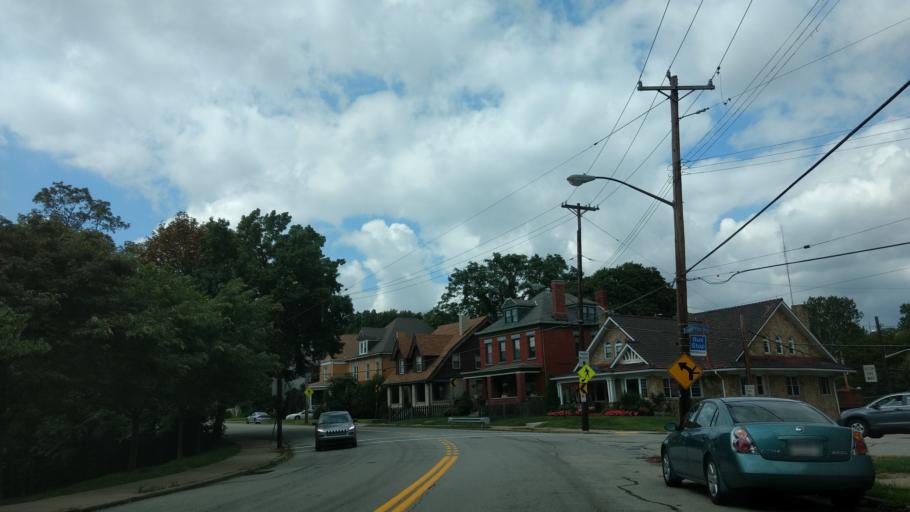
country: US
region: Pennsylvania
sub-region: Allegheny County
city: Millvale
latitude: 40.4840
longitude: -80.0133
